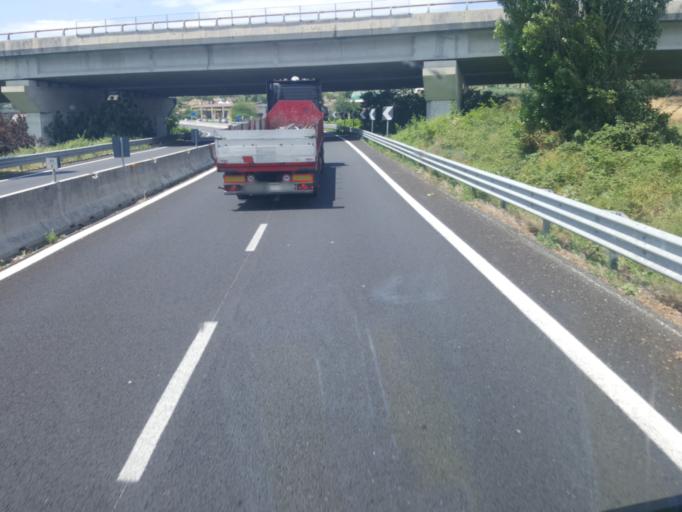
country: IT
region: Latium
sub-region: Citta metropolitana di Roma Capitale
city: Fiano Romano
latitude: 42.1498
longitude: 12.6272
